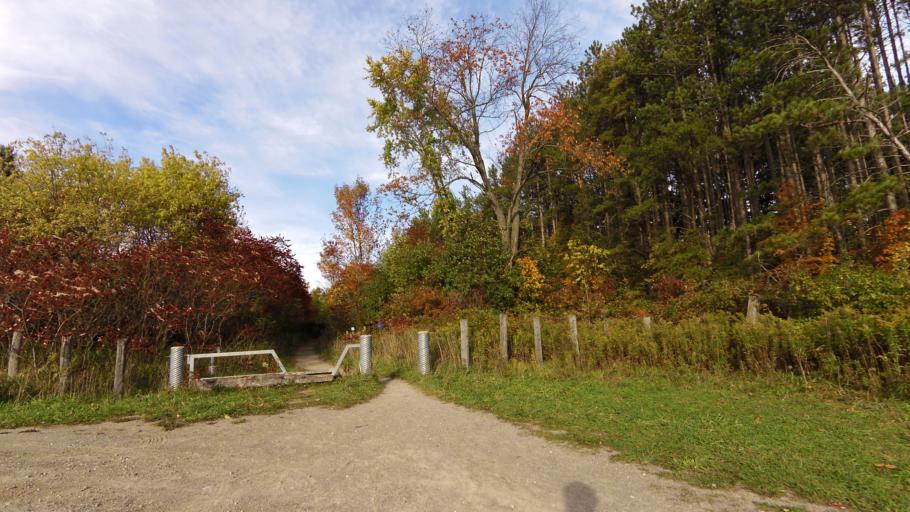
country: CA
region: Ontario
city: Orangeville
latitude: 43.8175
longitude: -80.0262
